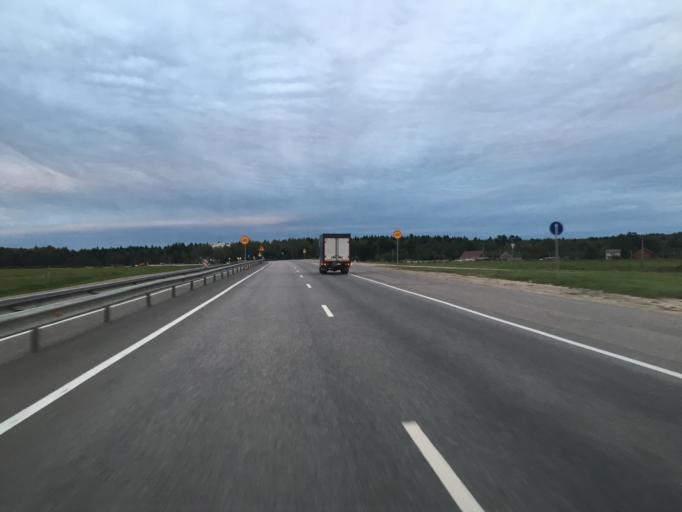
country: RU
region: Kaluga
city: Detchino
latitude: 54.6775
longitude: 36.2962
